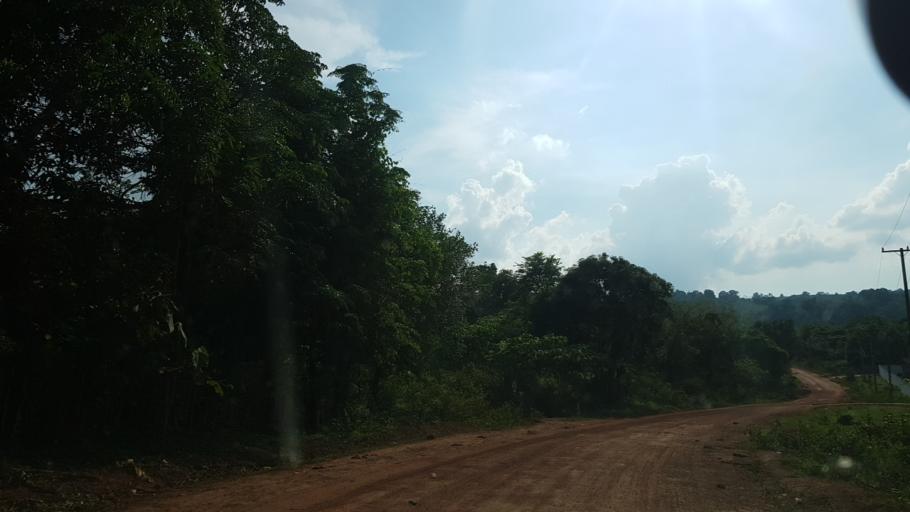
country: LA
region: Vientiane
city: Muang Phon-Hong
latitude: 18.3501
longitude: 102.2711
